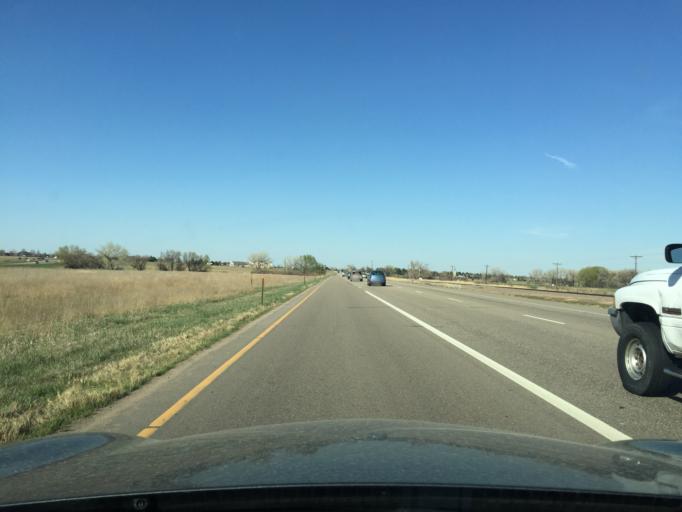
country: US
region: Colorado
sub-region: Boulder County
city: Niwot
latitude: 40.1310
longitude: -105.1394
